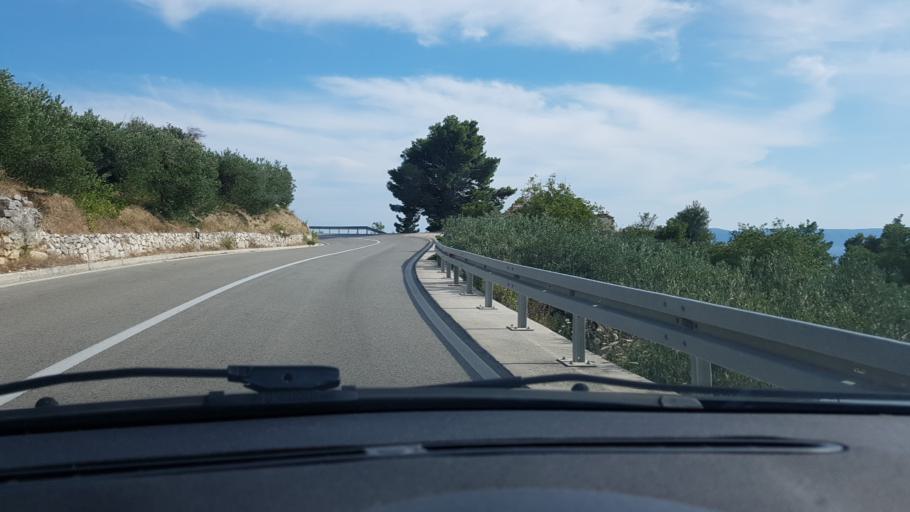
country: HR
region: Splitsko-Dalmatinska
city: Tucepi
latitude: 43.2794
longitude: 17.0467
